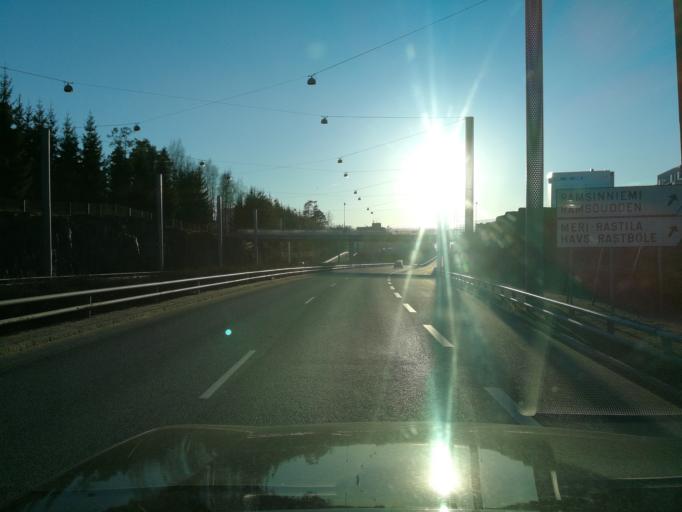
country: FI
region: Uusimaa
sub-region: Helsinki
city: Vantaa
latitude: 60.2046
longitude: 25.1251
